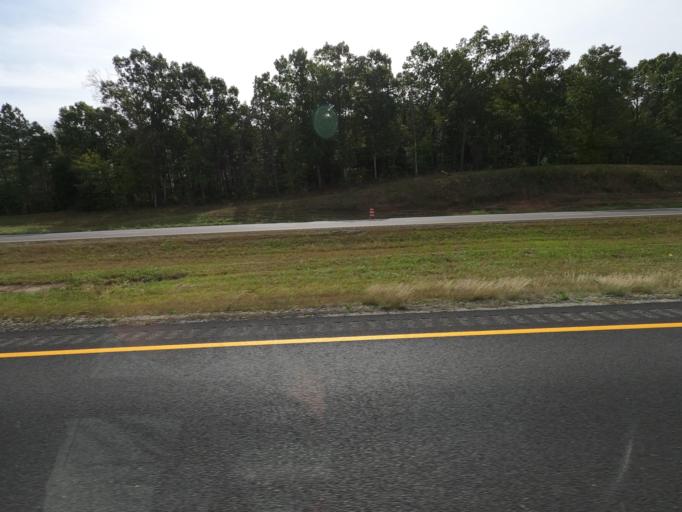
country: US
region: Tennessee
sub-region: Decatur County
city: Parsons
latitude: 35.8193
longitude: -88.1764
